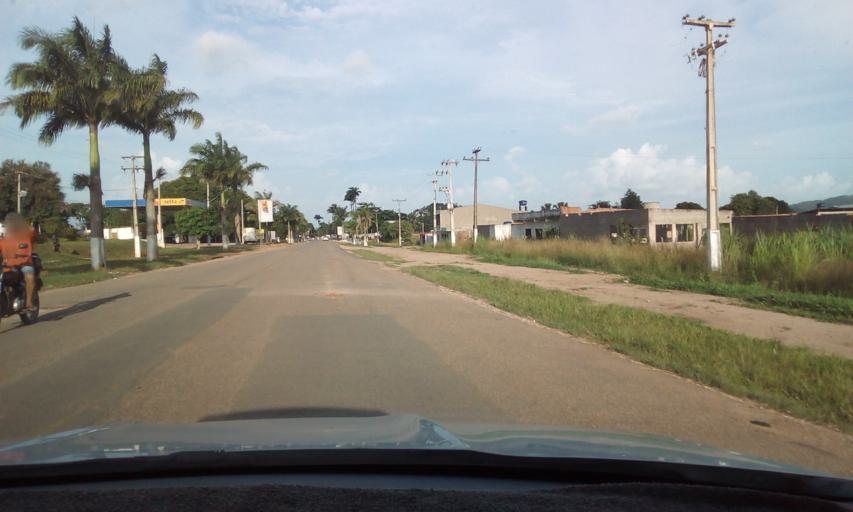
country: BR
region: Pernambuco
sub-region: Gloria Do Goita
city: Gloria do Goita
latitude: -7.9981
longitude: -35.2200
